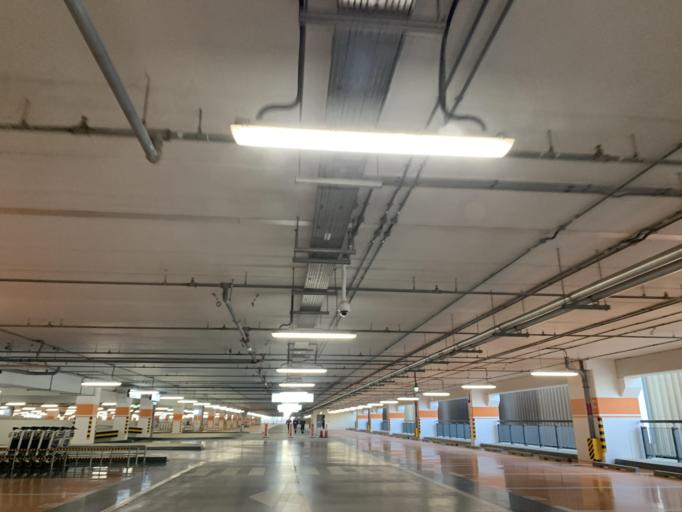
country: BH
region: Muharraq
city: Al Muharraq
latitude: 26.2674
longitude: 50.6293
